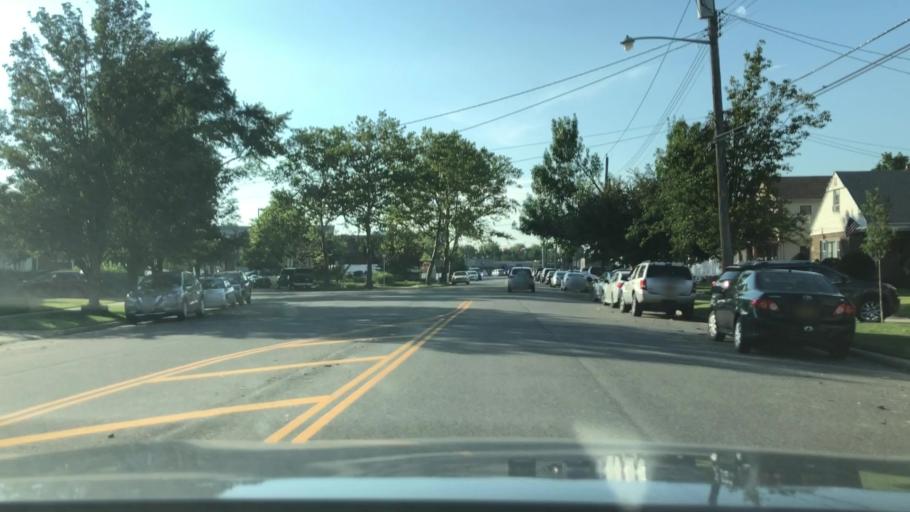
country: US
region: New York
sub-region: Nassau County
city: North New Hyde Park
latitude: 40.7394
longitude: -73.6963
